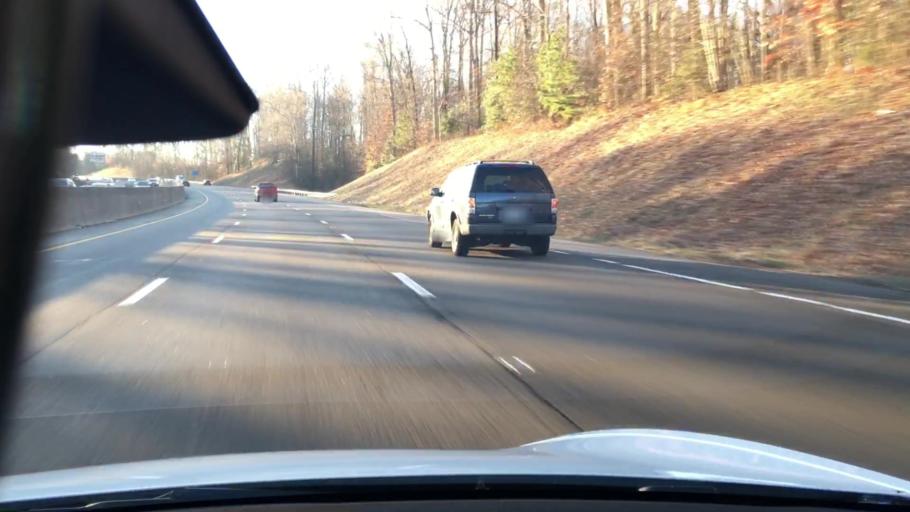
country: US
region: Virginia
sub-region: Chesterfield County
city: Bensley
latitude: 37.4562
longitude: -77.4946
